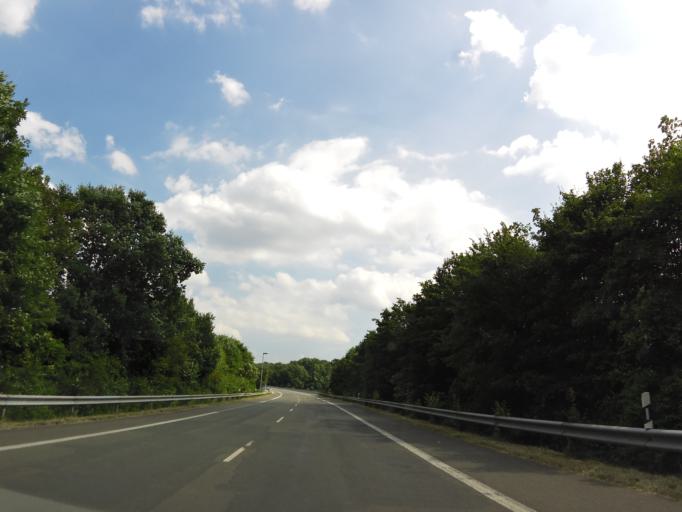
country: DE
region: North Rhine-Westphalia
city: Beverungen
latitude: 51.6396
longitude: 9.4021
